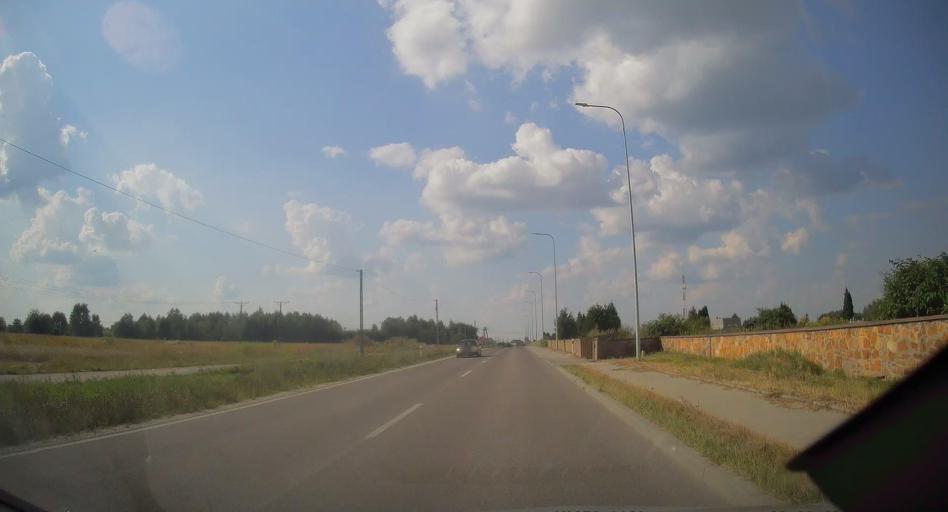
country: PL
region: Swietokrzyskie
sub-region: Powiat konecki
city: Radoszyce
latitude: 51.0671
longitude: 20.2712
